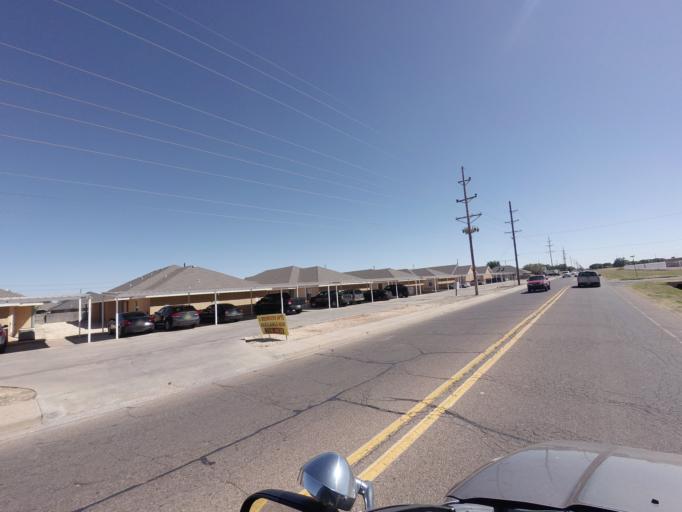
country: US
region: New Mexico
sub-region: Curry County
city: Clovis
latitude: 34.4176
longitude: -103.2318
